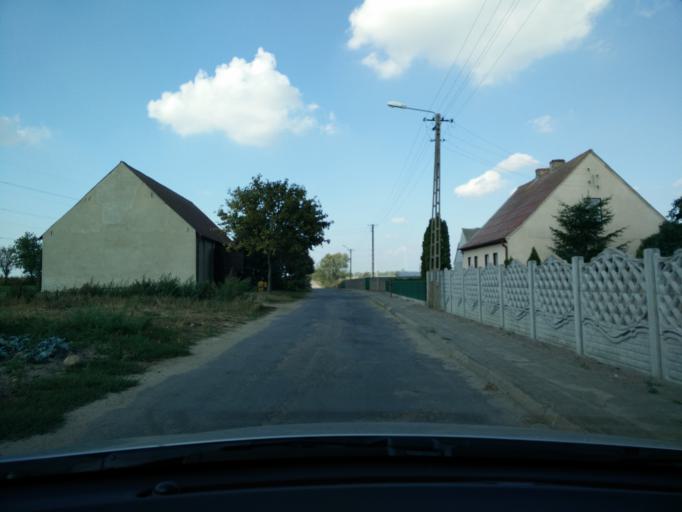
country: PL
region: Greater Poland Voivodeship
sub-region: Powiat sredzki
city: Sroda Wielkopolska
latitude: 52.2544
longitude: 17.2015
